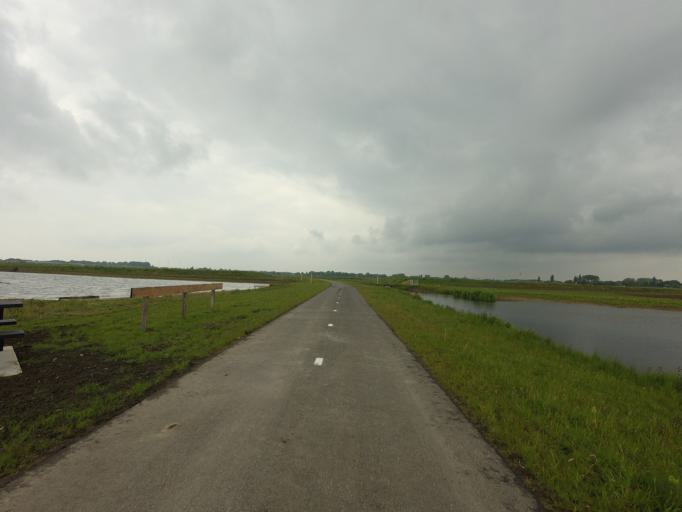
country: NL
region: South Holland
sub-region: Gemeente Zwijndrecht
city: Heerjansdam
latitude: 51.8461
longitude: 4.5889
